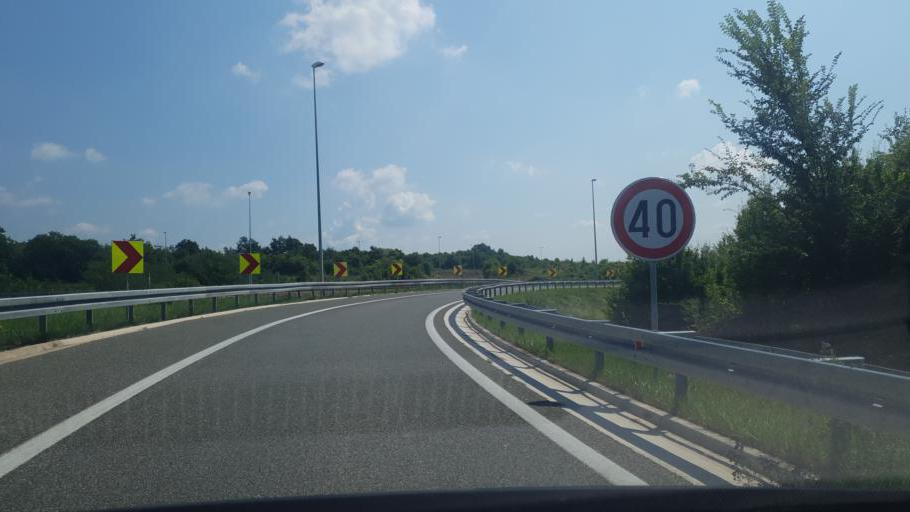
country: HR
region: Istarska
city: Vodnjan
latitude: 45.1143
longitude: 13.8118
